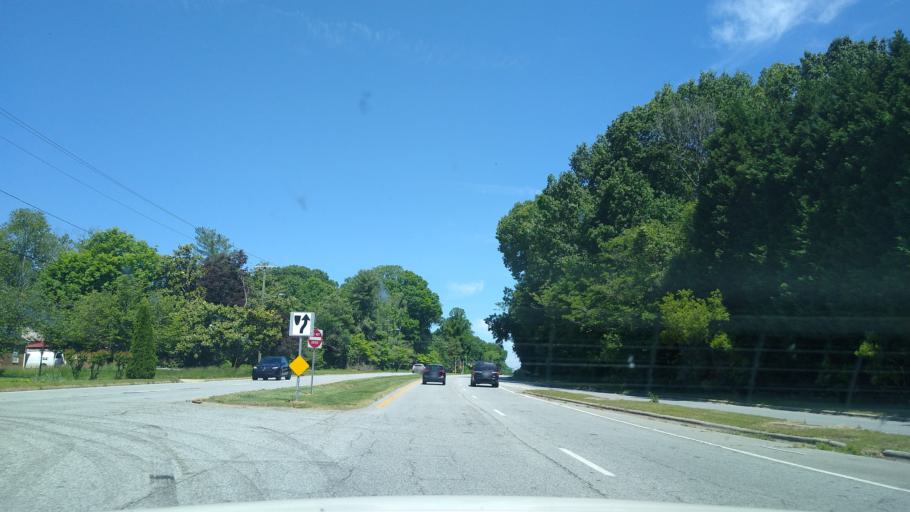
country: US
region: North Carolina
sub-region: Guilford County
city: Greensboro
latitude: 36.0897
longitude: -79.8270
